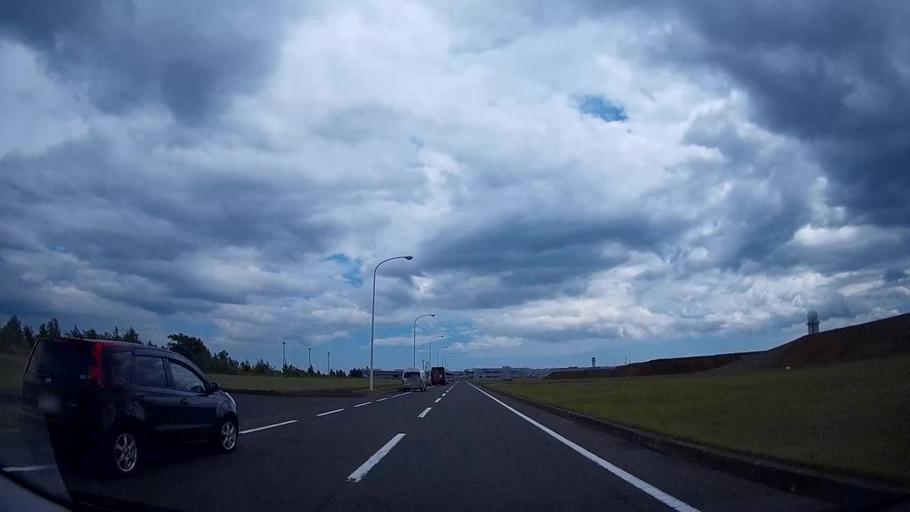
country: JP
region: Hokkaido
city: Chitose
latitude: 42.7999
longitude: 141.6798
